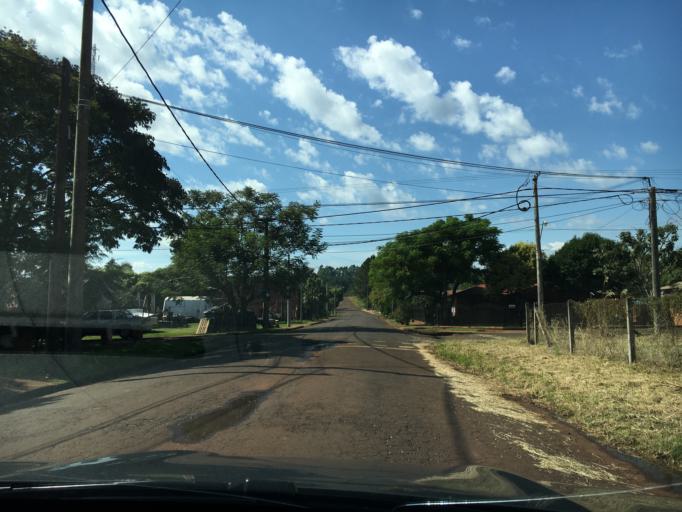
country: AR
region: Misiones
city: Puerto Rico
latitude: -26.8167
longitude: -55.0207
